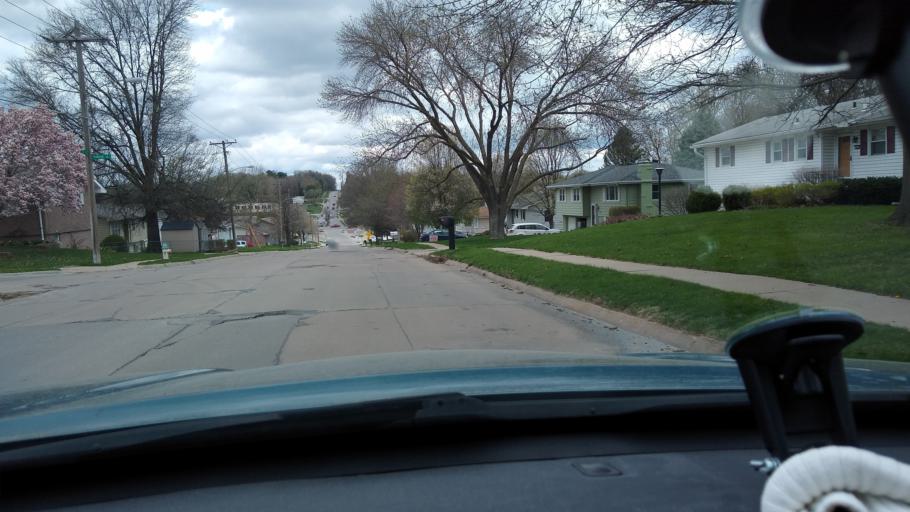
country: US
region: Nebraska
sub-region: Douglas County
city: Ralston
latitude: 41.2307
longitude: -96.0910
